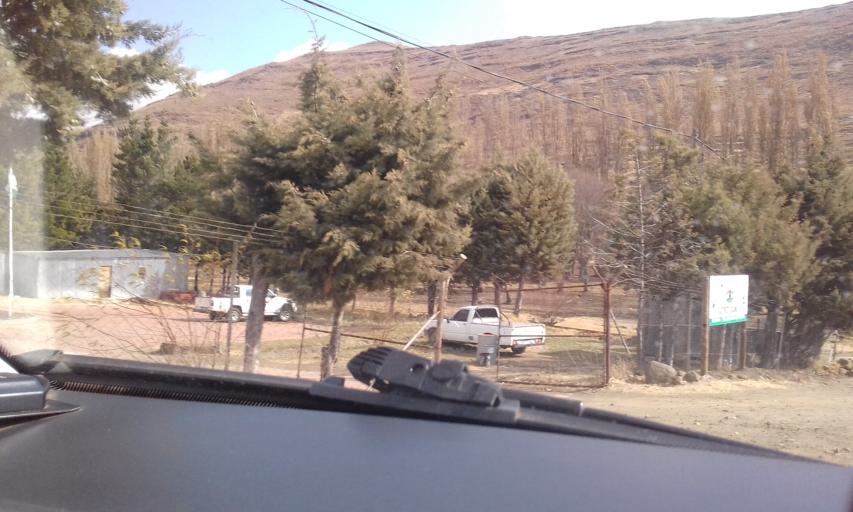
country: LS
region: Thaba-Tseka
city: Thaba-Tseka
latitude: -29.5237
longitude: 28.6034
